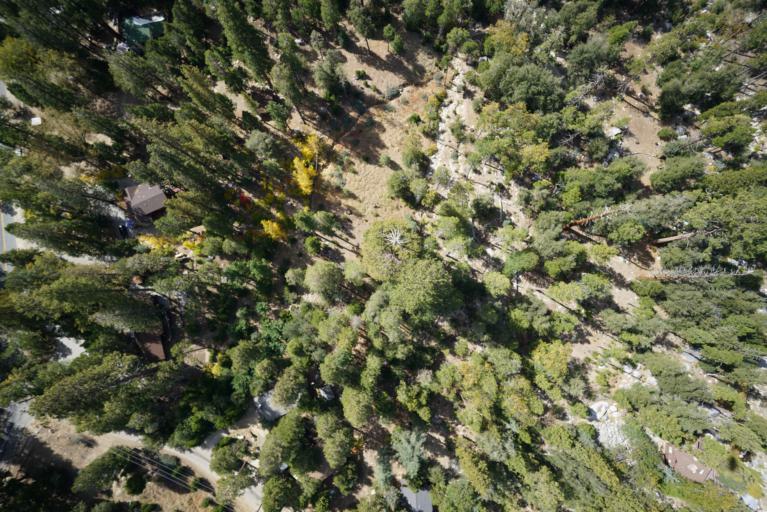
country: US
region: California
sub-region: Riverside County
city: Idyllwild
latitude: 33.7598
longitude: -116.6990
